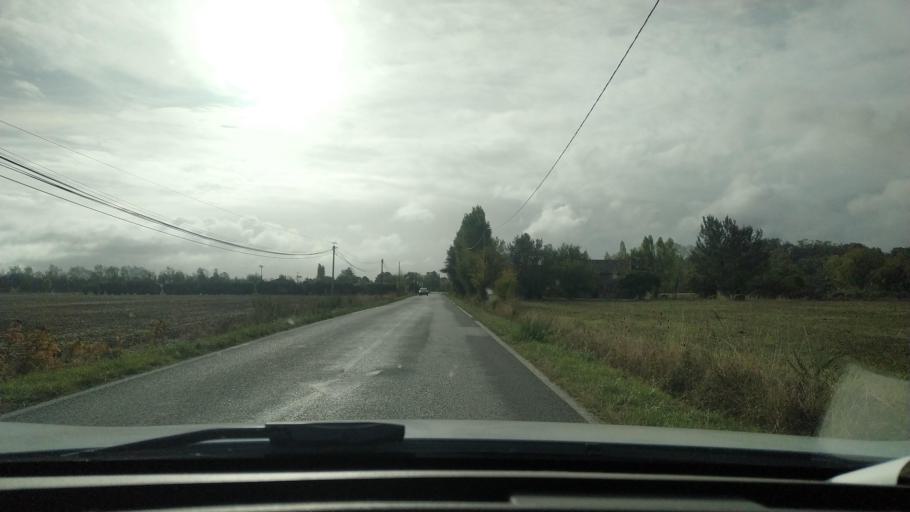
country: FR
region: Midi-Pyrenees
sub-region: Departement de la Haute-Garonne
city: Auterive
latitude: 43.3183
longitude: 1.4513
